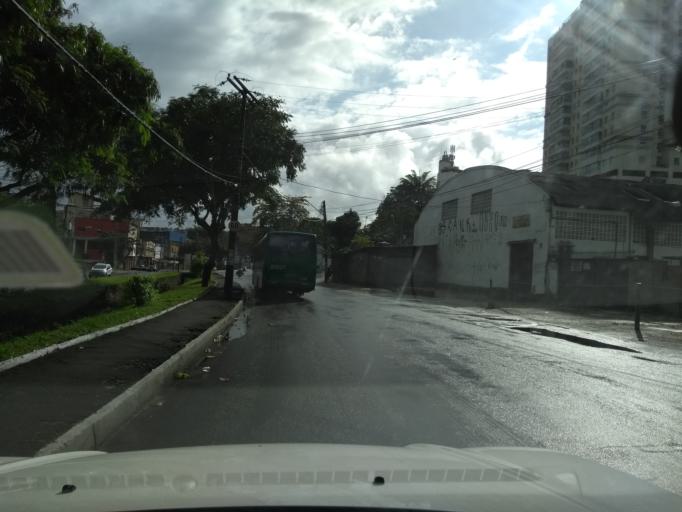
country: BR
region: Bahia
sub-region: Salvador
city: Salvador
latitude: -12.9681
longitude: -38.4946
